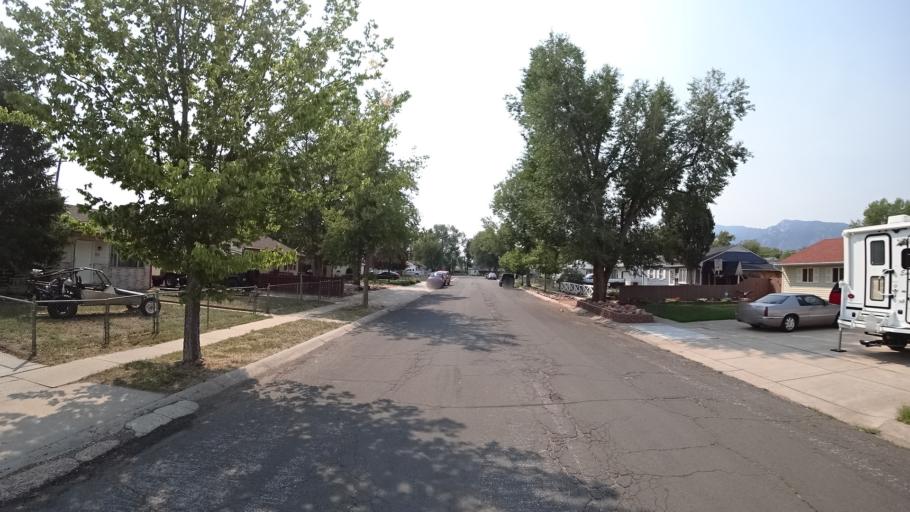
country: US
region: Colorado
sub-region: El Paso County
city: Colorado Springs
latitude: 38.8049
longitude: -104.8086
